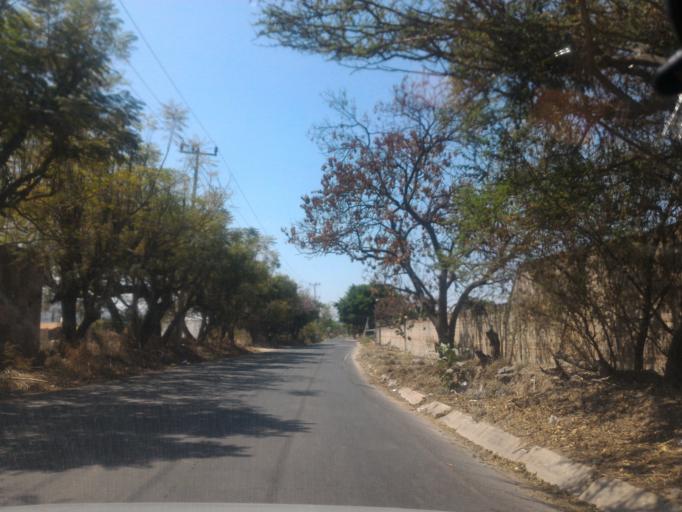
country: MX
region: Jalisco
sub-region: San Pedro Tlaquepaque
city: Santa Anita
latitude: 20.5538
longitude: -103.4306
